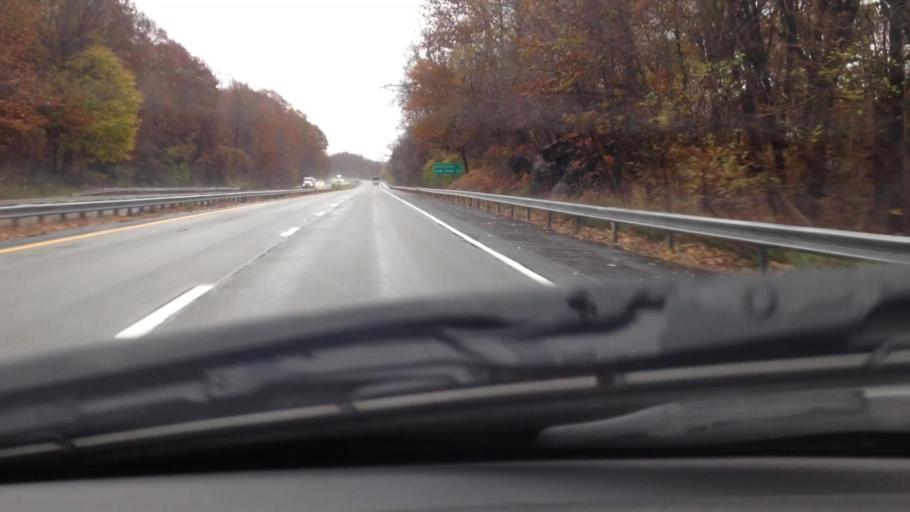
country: US
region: New York
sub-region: Westchester County
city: Montrose
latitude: 41.2592
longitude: -73.9305
